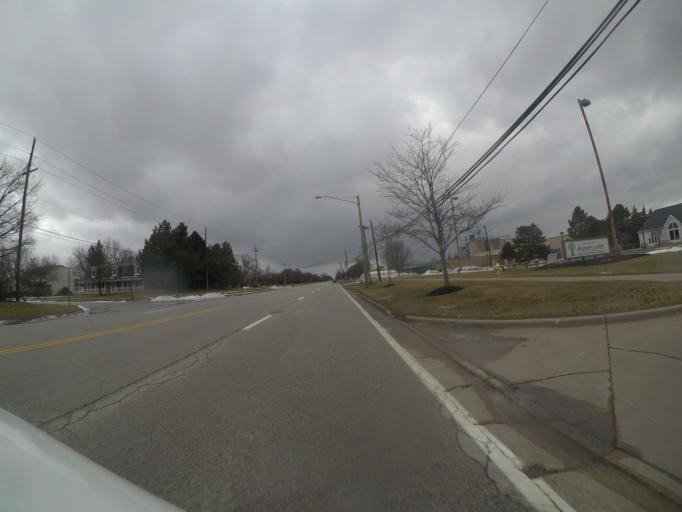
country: US
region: Ohio
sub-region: Wood County
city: Perrysburg
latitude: 41.5645
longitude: -83.6084
